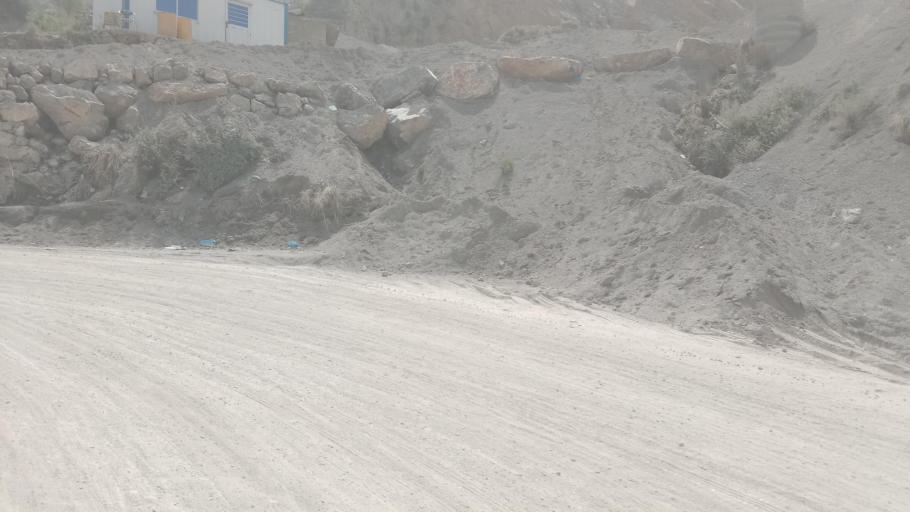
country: PK
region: Khyber Pakhtunkhwa
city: Abbottabad
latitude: 34.1612
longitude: 73.2809
